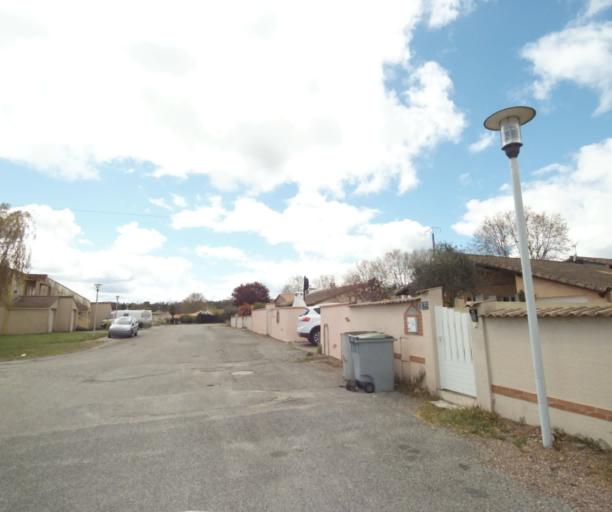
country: FR
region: Midi-Pyrenees
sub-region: Departement de l'Ariege
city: Saverdun
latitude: 43.2353
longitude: 1.5835
